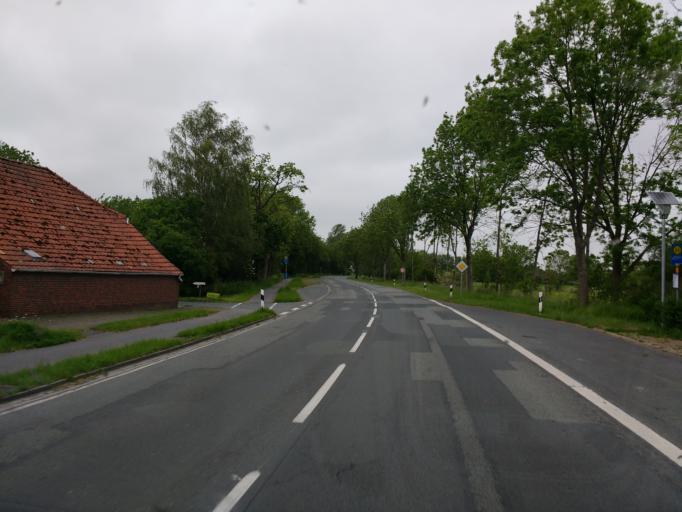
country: DE
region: Lower Saxony
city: Jever
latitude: 53.6271
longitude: 7.9272
